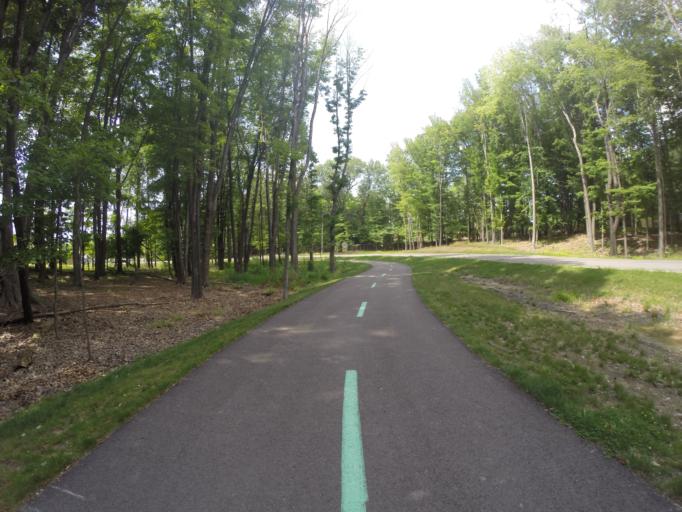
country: US
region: Ohio
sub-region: Cuyahoga County
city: Seven Hills
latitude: 41.3895
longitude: -81.6943
